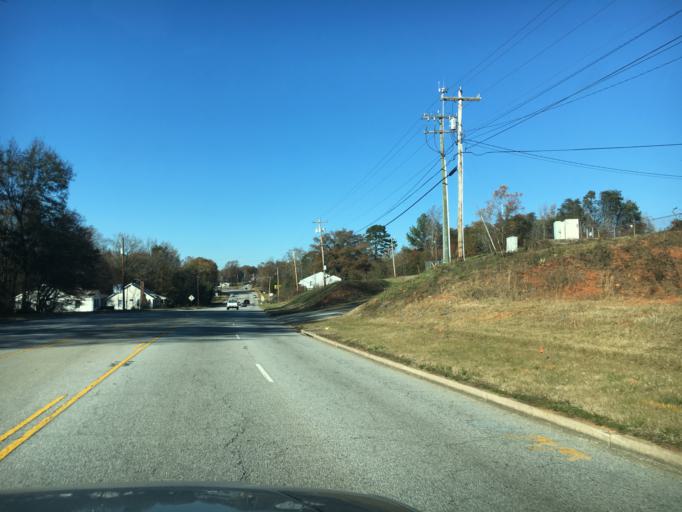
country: US
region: South Carolina
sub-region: Greenville County
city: Greer
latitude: 34.9154
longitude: -82.2115
